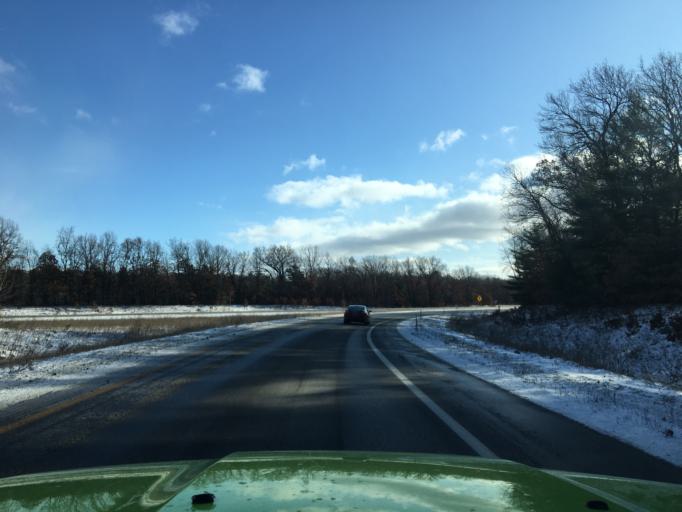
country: US
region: Michigan
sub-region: Montcalm County
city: Howard City
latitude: 43.4228
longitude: -85.4987
